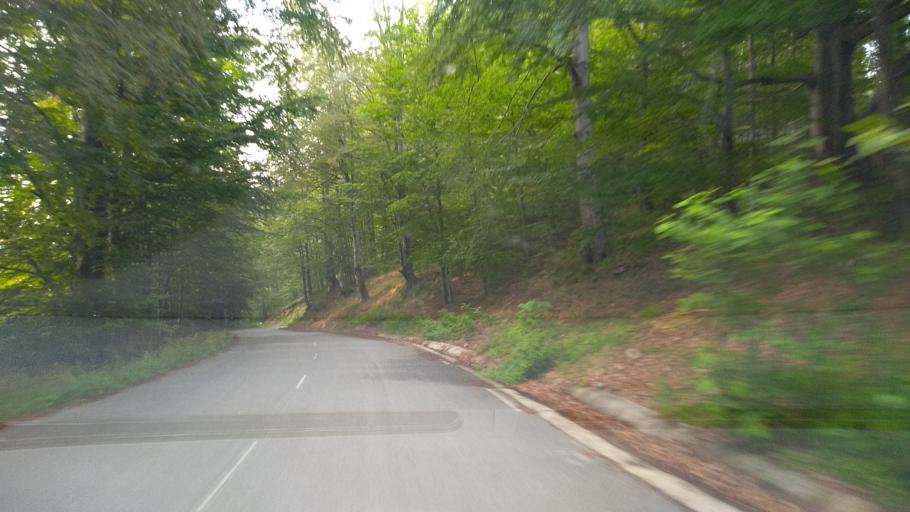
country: RO
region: Hunedoara
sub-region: Municipiul  Vulcan
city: Jiu-Paroseni
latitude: 45.3412
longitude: 23.2921
